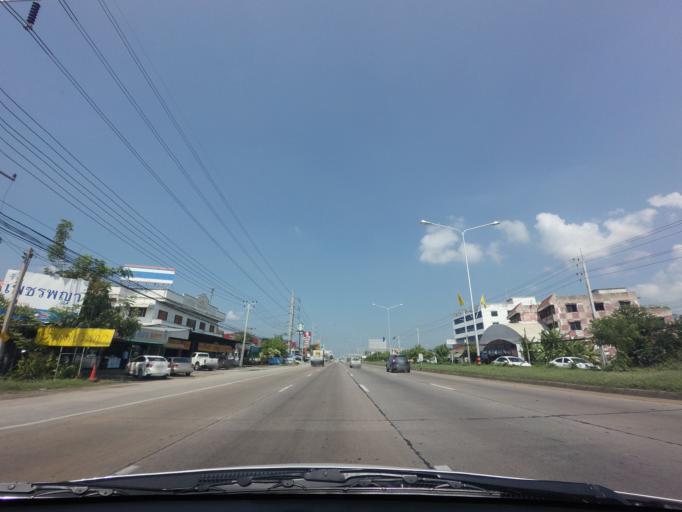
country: TH
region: Nakhon Pathom
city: Nakhon Chai Si
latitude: 13.7717
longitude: 100.1809
